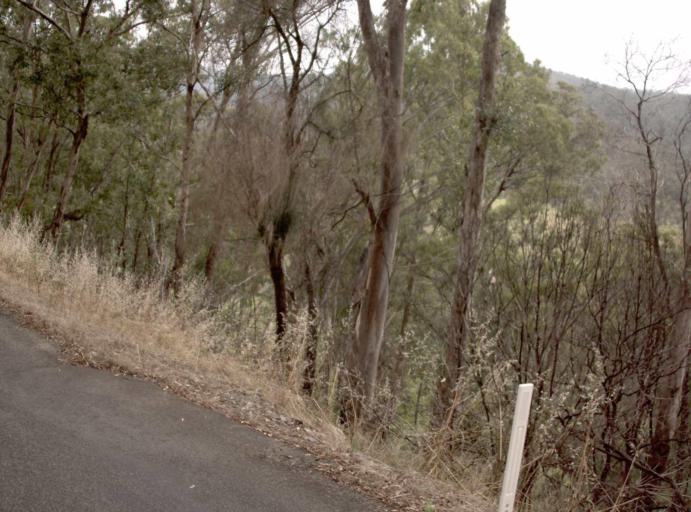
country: AU
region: Victoria
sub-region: Wellington
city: Heyfield
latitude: -37.8083
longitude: 146.6717
